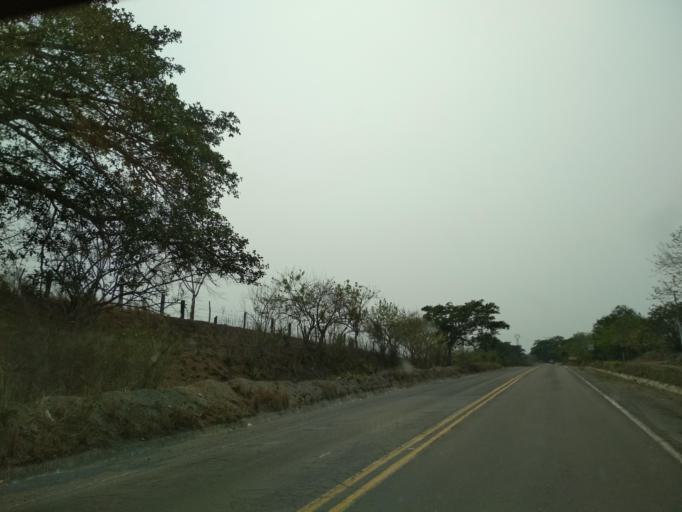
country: MX
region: Veracruz
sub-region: Veracruz
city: Delfino Victoria (Santa Fe)
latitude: 19.2029
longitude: -96.3119
